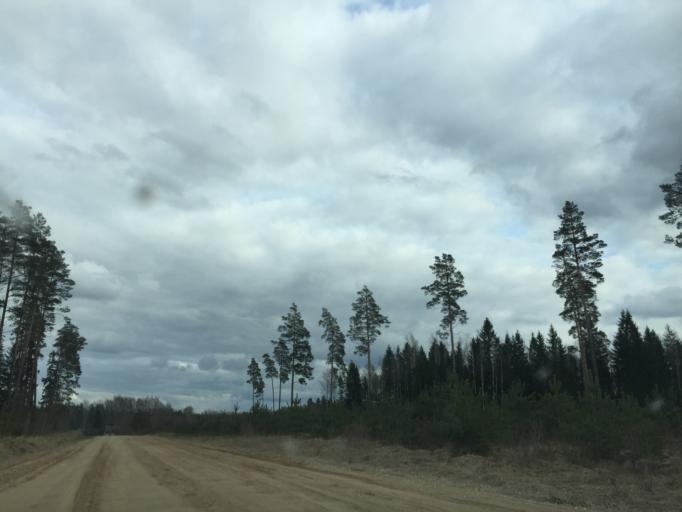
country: LV
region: Ogre
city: Jumprava
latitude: 56.5477
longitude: 24.8538
